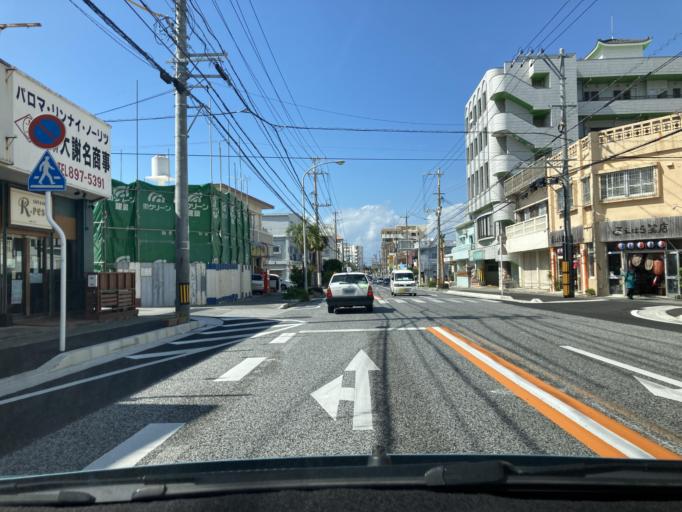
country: JP
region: Okinawa
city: Ginowan
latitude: 26.2609
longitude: 127.7435
